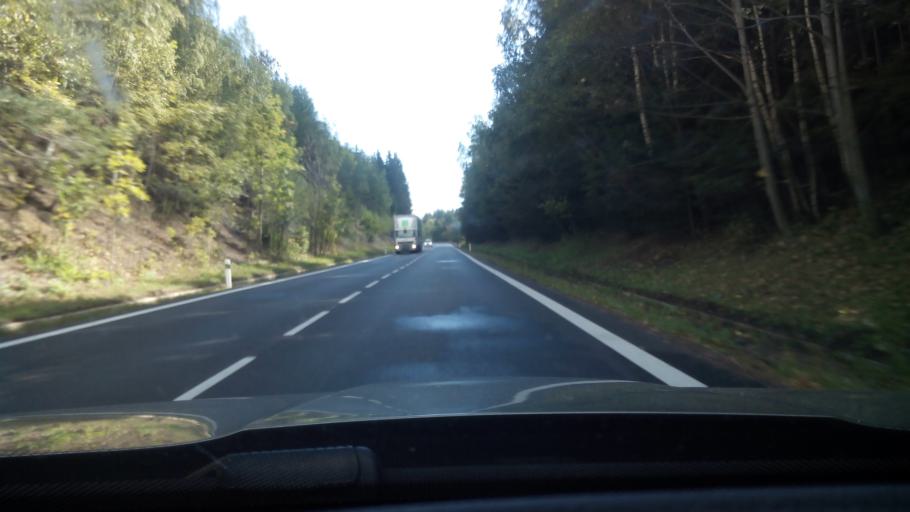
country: CZ
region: Jihocesky
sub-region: Okres Prachatice
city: Zdikov
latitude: 49.0709
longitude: 13.7147
